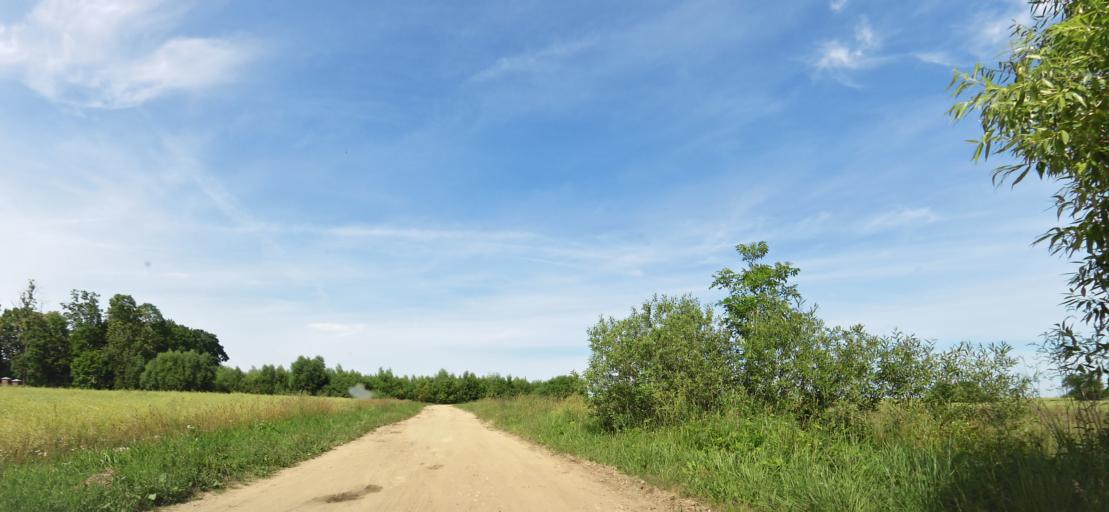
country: LT
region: Panevezys
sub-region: Panevezys City
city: Panevezys
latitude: 55.9065
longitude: 24.2854
